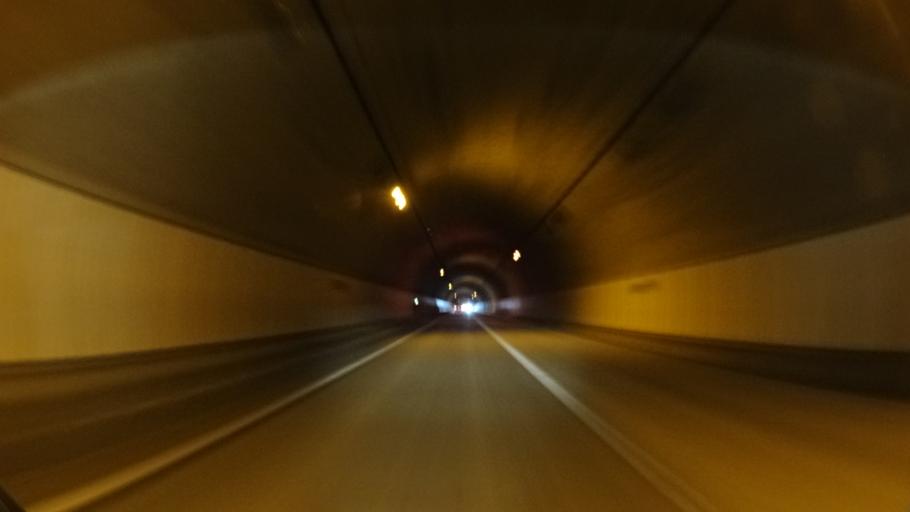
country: JP
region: Ehime
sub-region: Nishiuwa-gun
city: Ikata-cho
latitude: 33.5099
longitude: 132.3956
